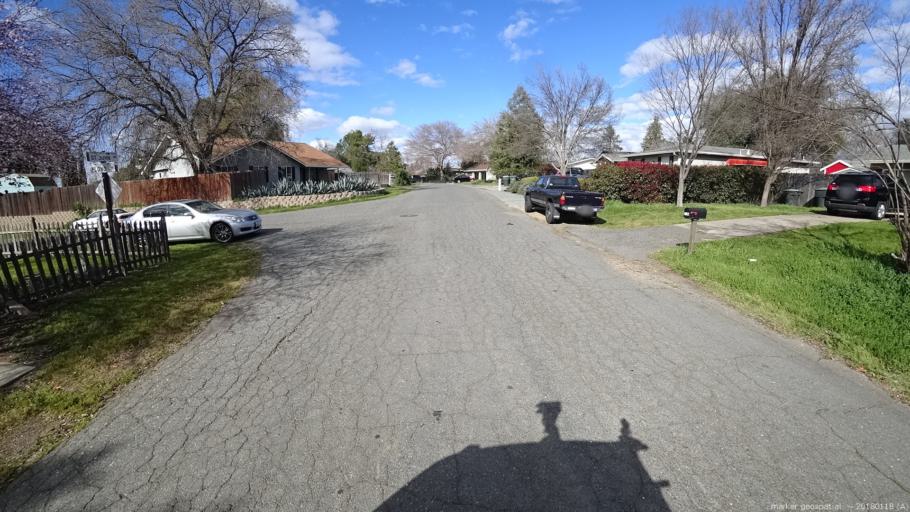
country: US
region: California
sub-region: Sacramento County
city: Orangevale
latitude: 38.6985
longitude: -121.2074
